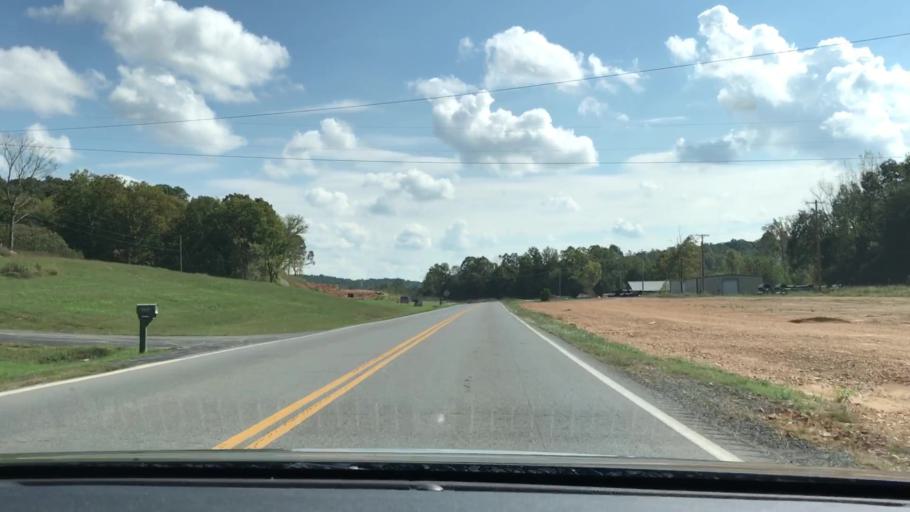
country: US
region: Kentucky
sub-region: Trigg County
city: Cadiz
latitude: 36.8054
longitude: -87.9232
